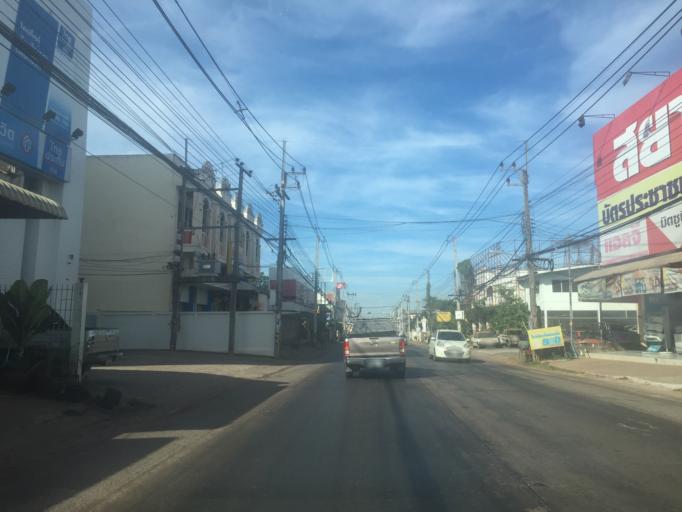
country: TH
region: Changwat Udon Thani
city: Kumphawapi
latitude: 17.1109
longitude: 103.0137
